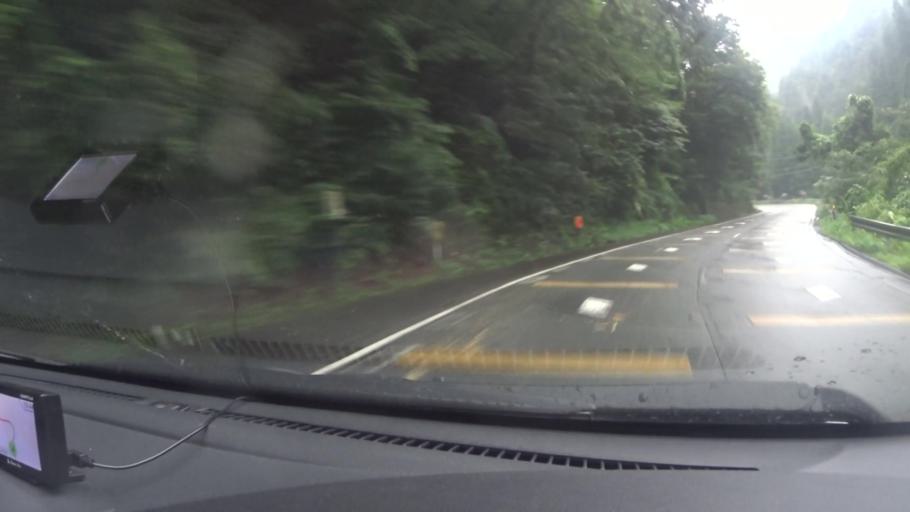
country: JP
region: Kyoto
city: Ayabe
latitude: 35.2401
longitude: 135.3009
